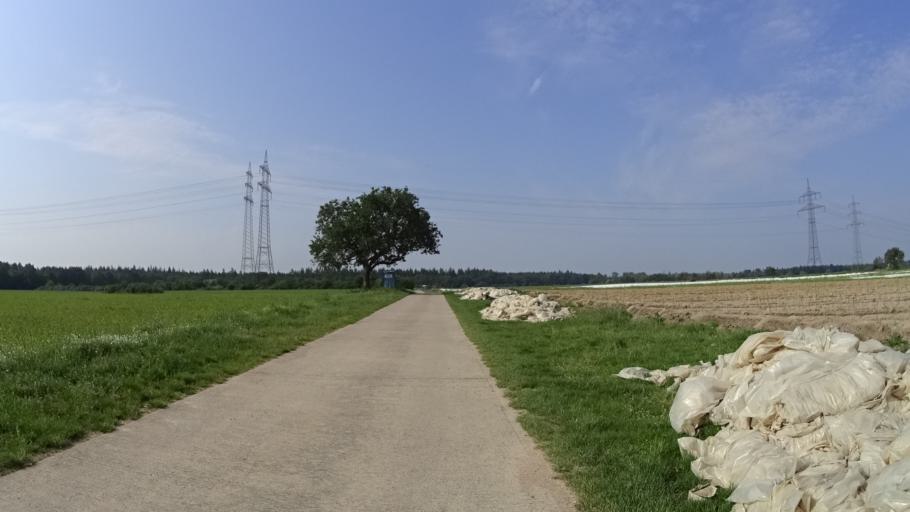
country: DE
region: Baden-Wuerttemberg
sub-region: Karlsruhe Region
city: Hambrucken
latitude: 49.2086
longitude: 8.5232
